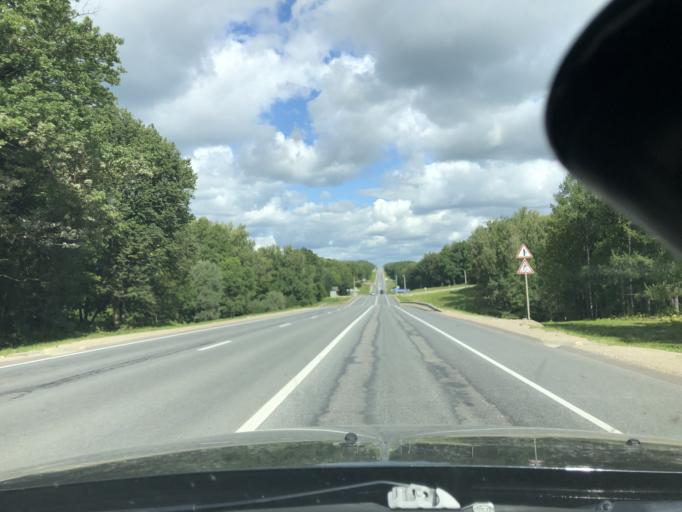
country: RU
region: Tula
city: Gorelki
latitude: 54.3185
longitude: 37.5616
